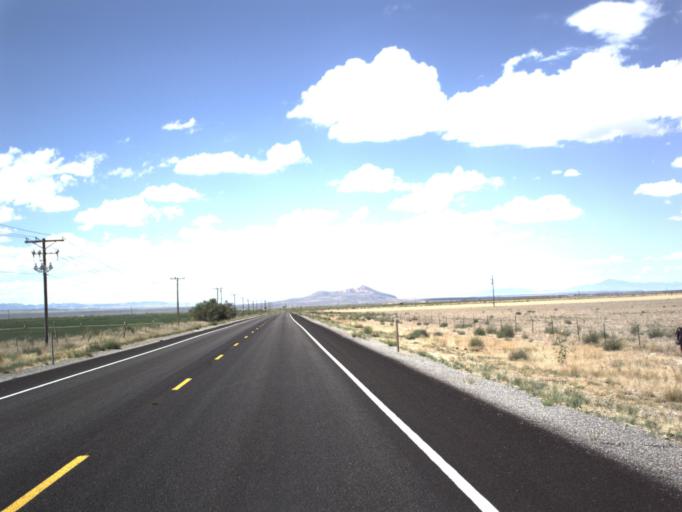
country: US
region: Utah
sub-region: Millard County
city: Fillmore
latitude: 39.1181
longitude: -112.3413
